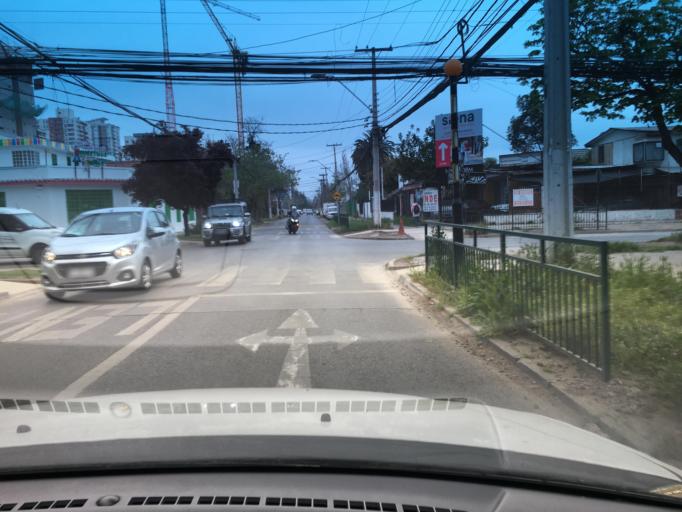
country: CL
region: Santiago Metropolitan
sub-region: Provincia de Santiago
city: Villa Presidente Frei, Nunoa, Santiago, Chile
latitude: -33.4764
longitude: -70.6014
